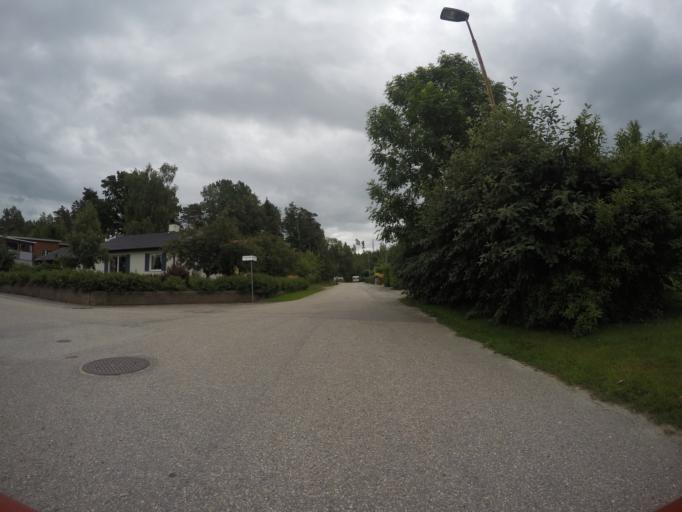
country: SE
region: Vaestra Goetaland
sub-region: Trollhattan
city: Sjuntorp
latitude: 58.2026
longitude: 12.2404
